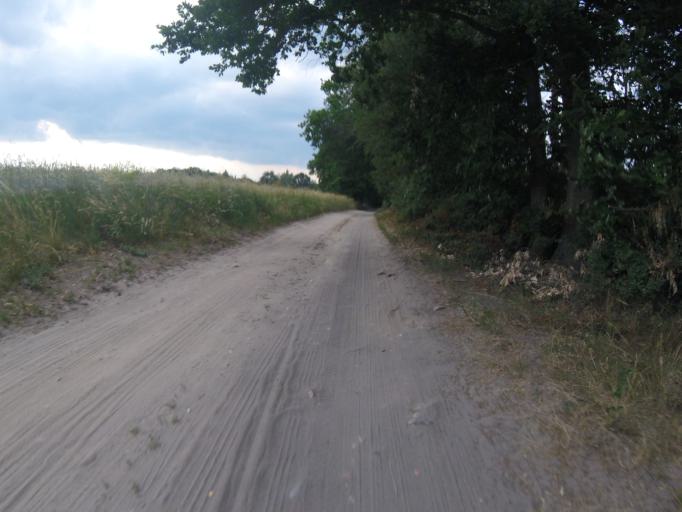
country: DE
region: Brandenburg
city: Bestensee
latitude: 52.2585
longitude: 13.6178
